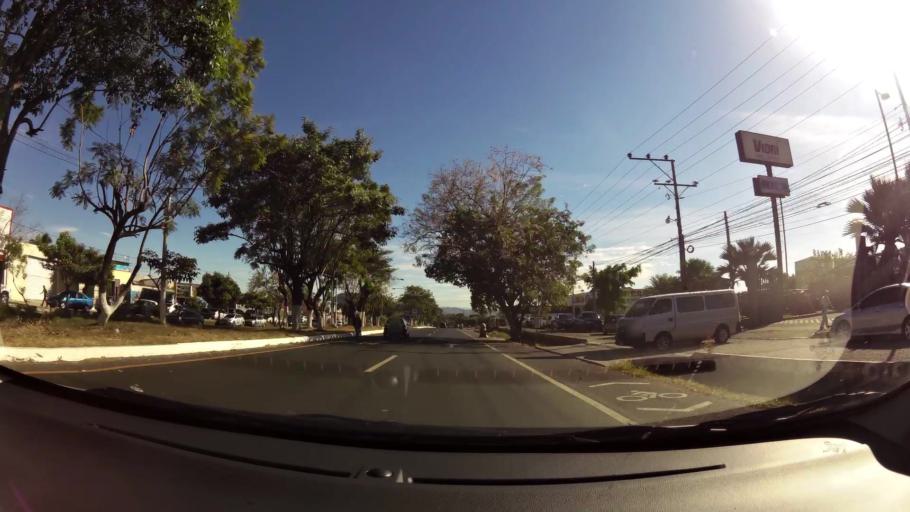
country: SV
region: Santa Ana
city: Santa Ana
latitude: 13.9774
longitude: -89.5584
